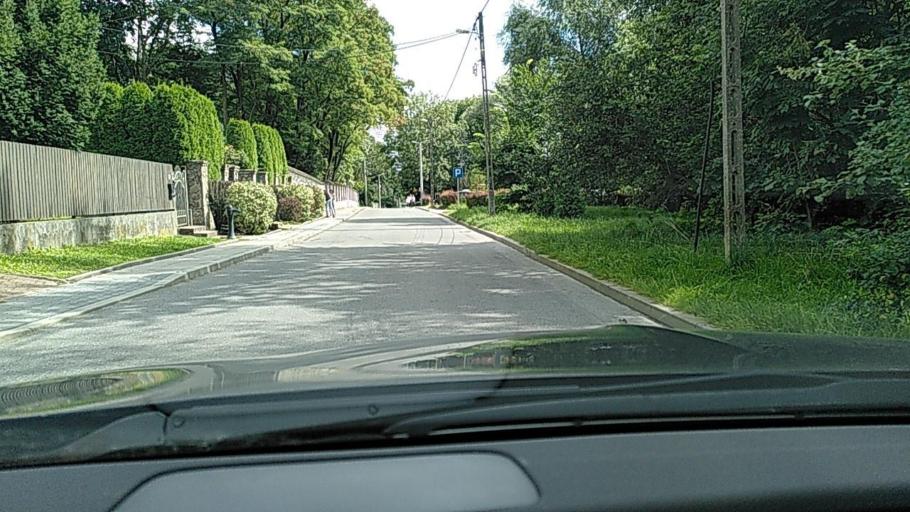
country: PL
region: Lesser Poland Voivodeship
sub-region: Powiat krakowski
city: Rzaska
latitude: 50.0878
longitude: 19.8755
